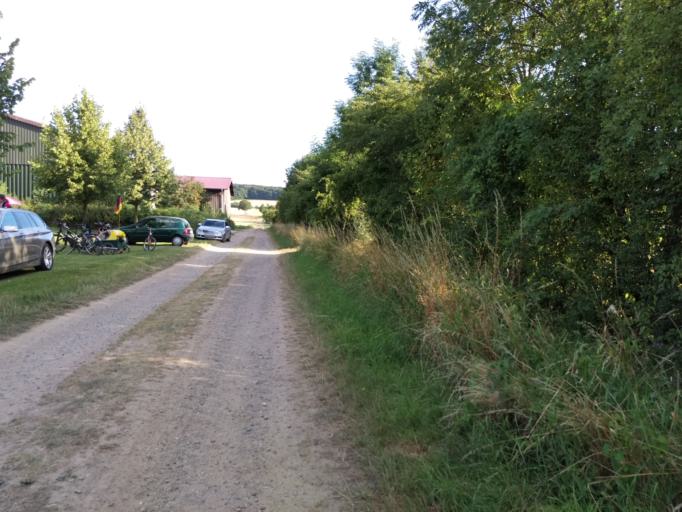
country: DE
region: Lower Saxony
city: Schellerten
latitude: 52.1346
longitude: 10.0704
